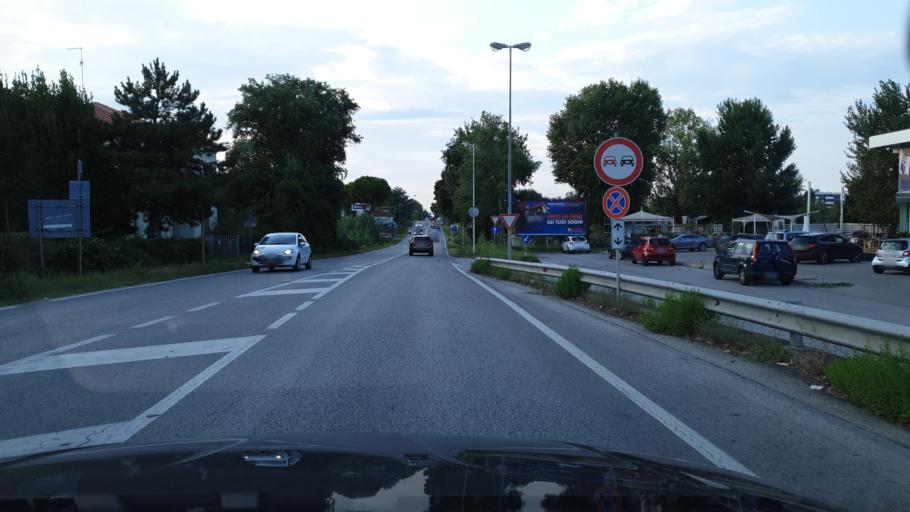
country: IT
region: Emilia-Romagna
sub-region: Provincia di Rimini
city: Rivazzurra
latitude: 44.0193
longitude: 12.6265
